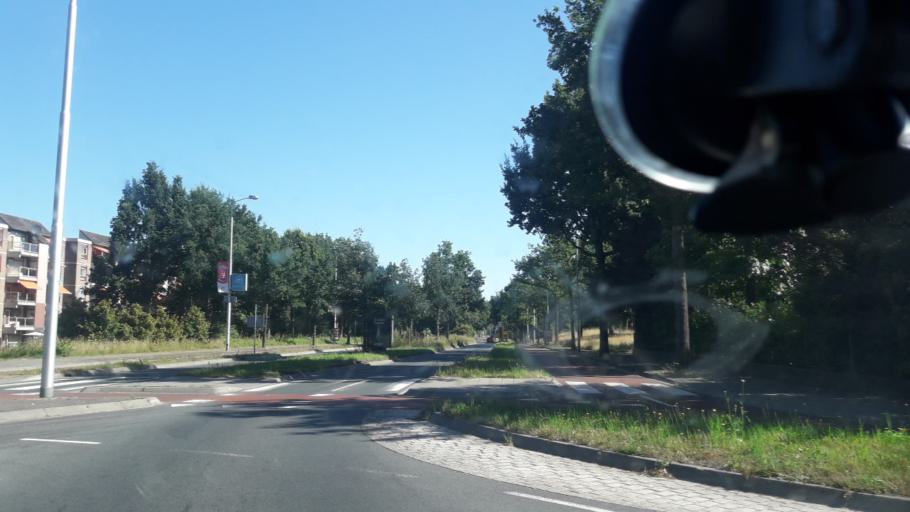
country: NL
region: Gelderland
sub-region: Gemeente Ede
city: Ede
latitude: 52.0472
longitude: 5.6748
